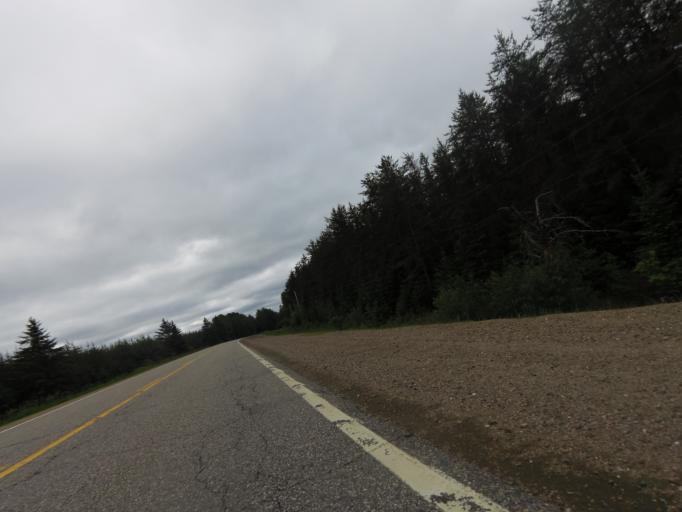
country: CA
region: Quebec
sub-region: Outaouais
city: Shawville
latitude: 45.8800
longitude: -76.3993
